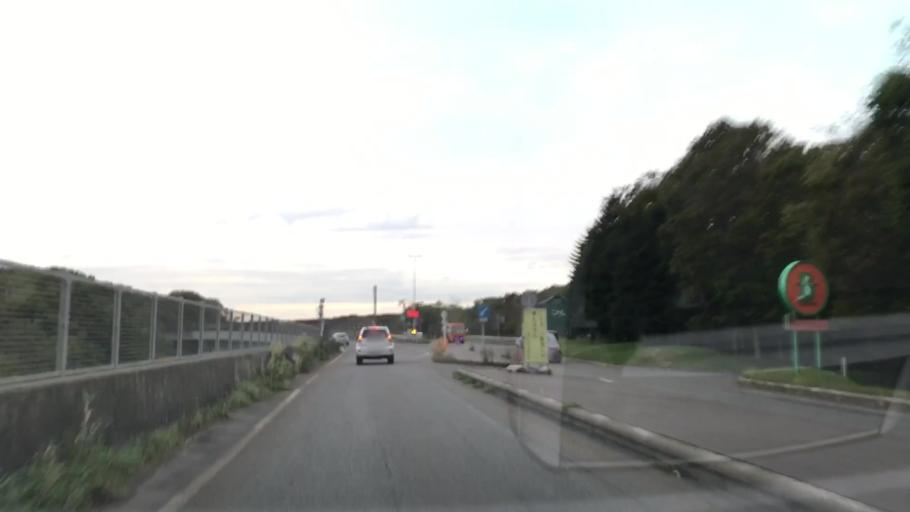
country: JP
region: Hokkaido
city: Tomakomai
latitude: 42.7073
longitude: 141.6608
